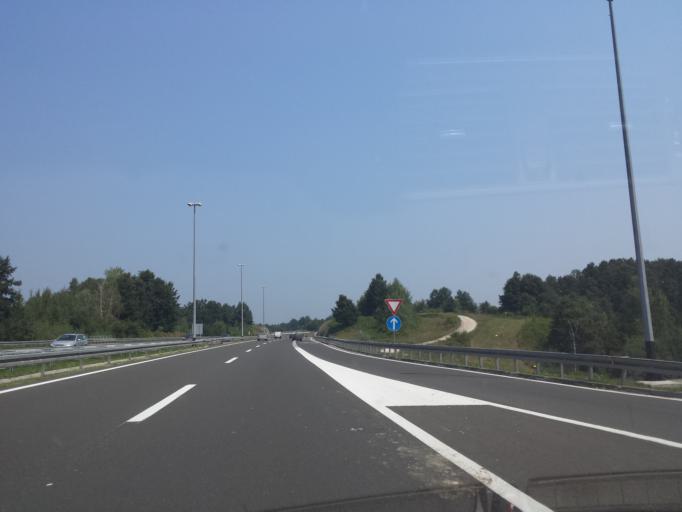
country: HR
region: Karlovacka
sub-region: Grad Ogulin
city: Ogulin
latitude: 45.3106
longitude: 15.2806
